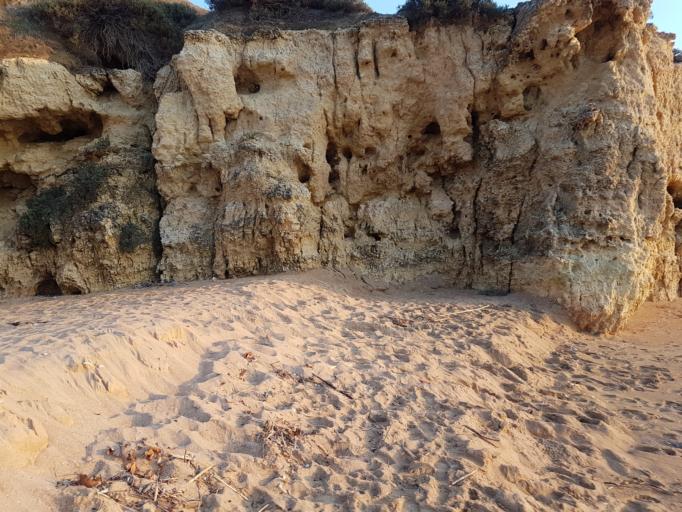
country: PT
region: Faro
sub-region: Albufeira
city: Albufeira
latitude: 37.0829
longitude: -8.2342
